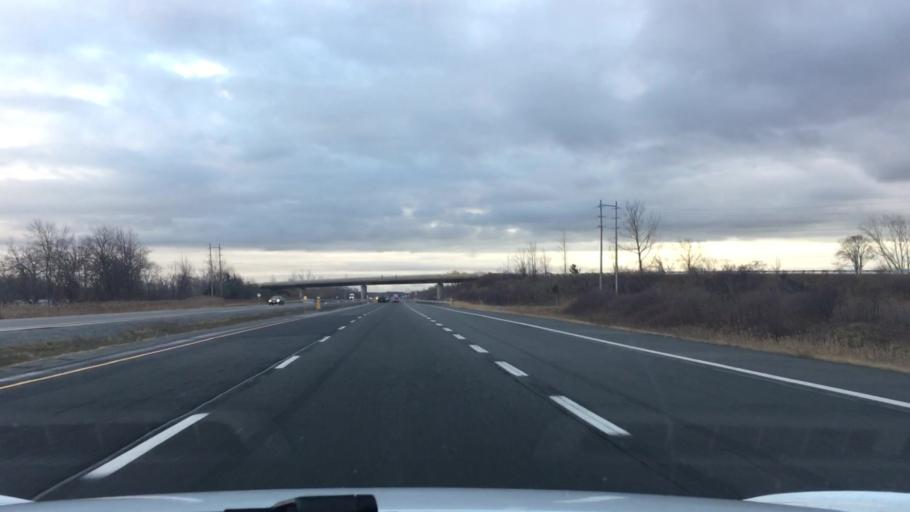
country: US
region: New York
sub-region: Erie County
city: Grandyle Village
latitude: 42.9650
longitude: -79.0245
